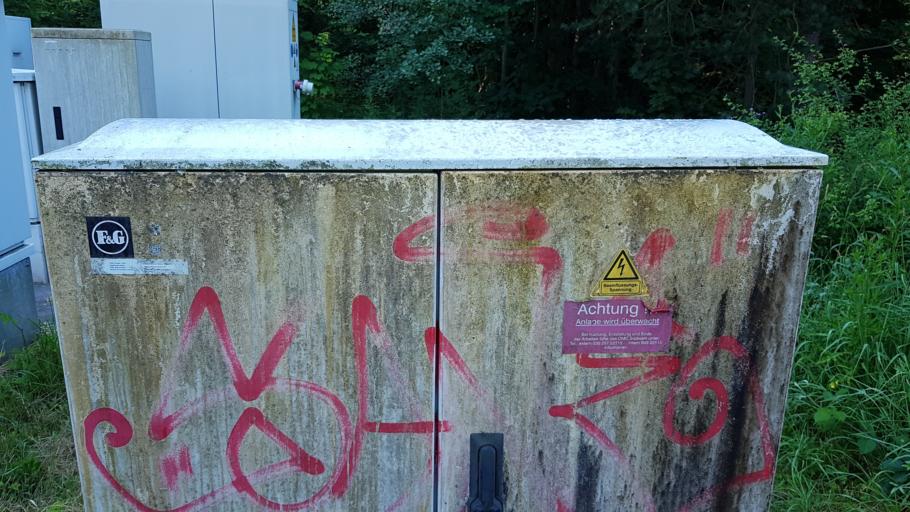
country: DE
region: Baden-Wuerttemberg
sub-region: Regierungsbezirk Stuttgart
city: Steinenbronn
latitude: 48.7081
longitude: 9.0995
